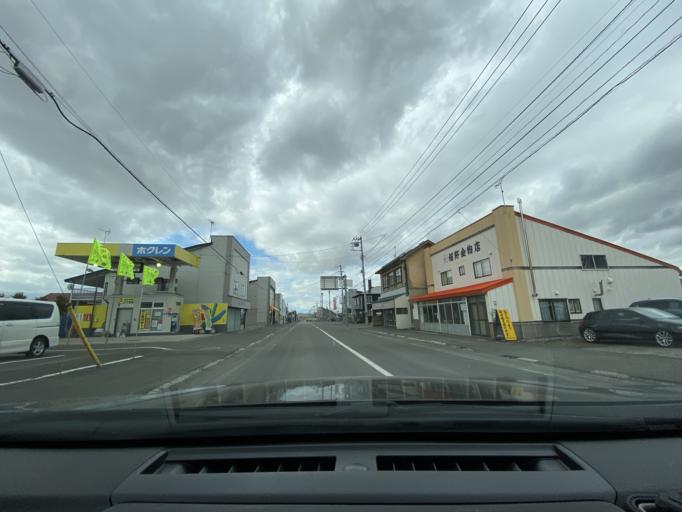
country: JP
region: Hokkaido
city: Nayoro
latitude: 44.1358
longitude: 142.4868
